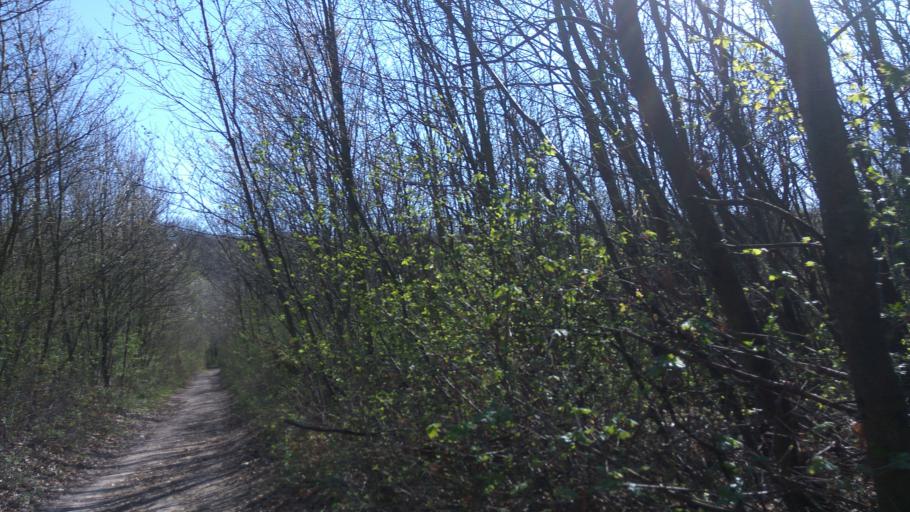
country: HU
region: Pest
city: Budakeszi
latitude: 47.4932
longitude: 18.9404
